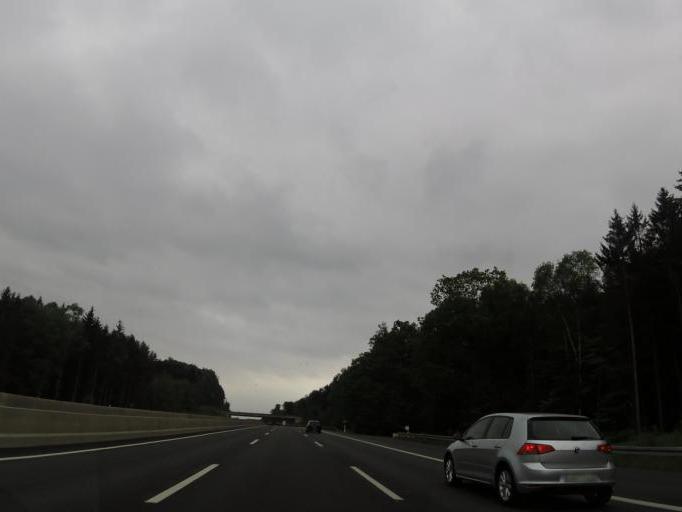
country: DE
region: Lower Saxony
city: Haverlah
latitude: 52.0426
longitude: 10.1799
